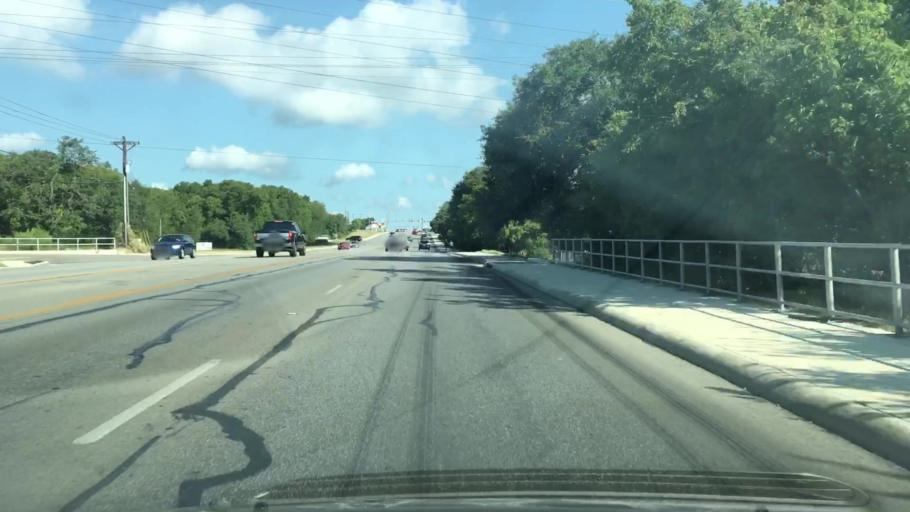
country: US
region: Texas
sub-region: Bexar County
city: Selma
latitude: 29.5938
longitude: -98.2727
